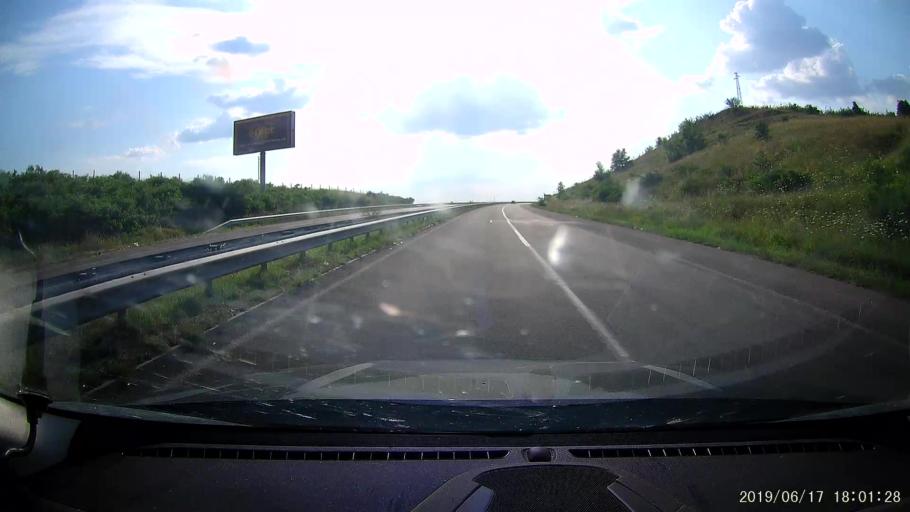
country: BG
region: Khaskovo
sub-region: Obshtina Svilengrad
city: Svilengrad
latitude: 41.7458
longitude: 26.2536
